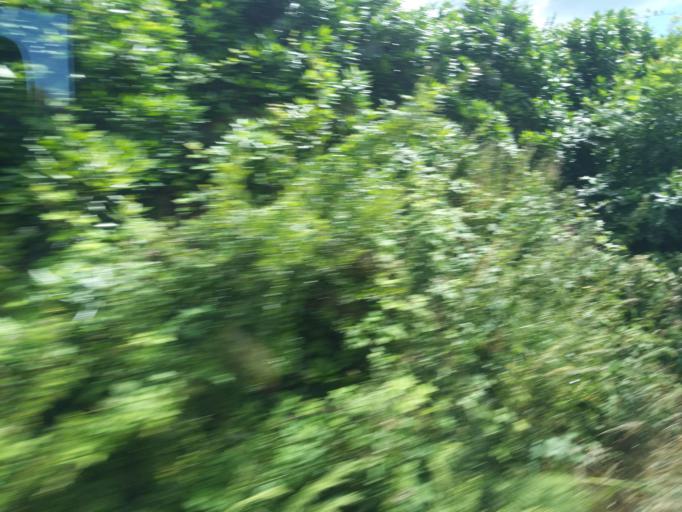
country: GB
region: England
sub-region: Cornwall
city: Par
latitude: 50.3651
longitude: -4.6881
